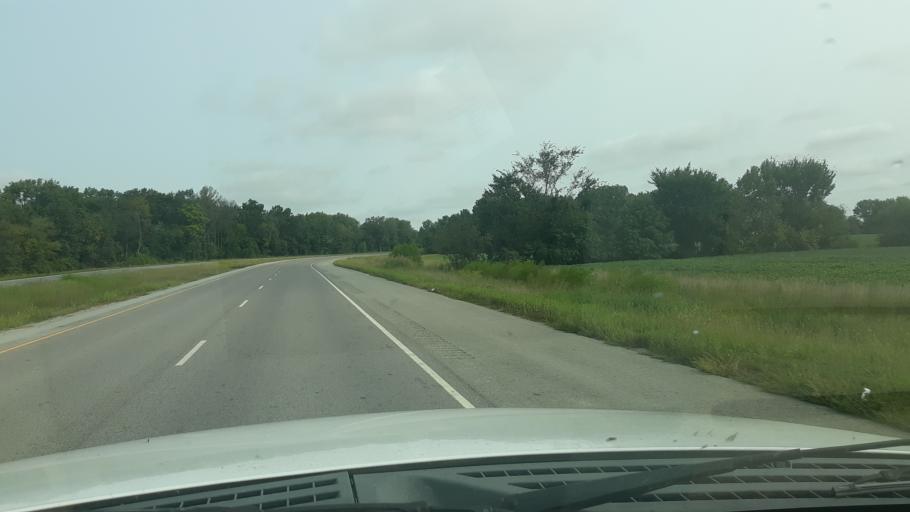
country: US
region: Illinois
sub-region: Saline County
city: Eldorado
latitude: 37.8207
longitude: -88.4270
